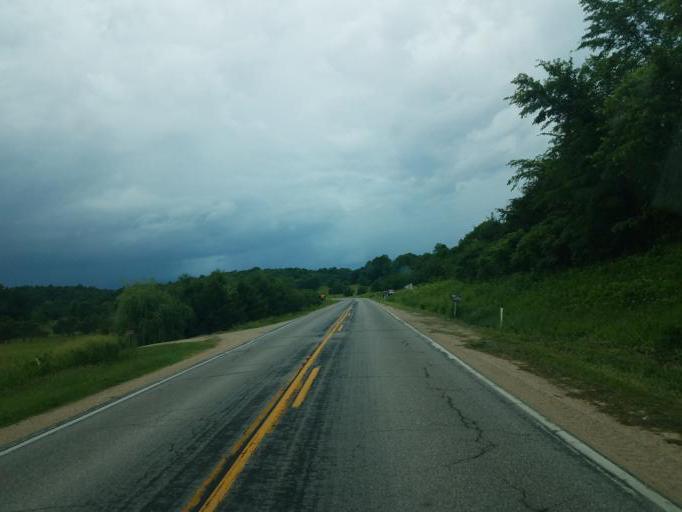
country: US
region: Wisconsin
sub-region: Vernon County
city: Hillsboro
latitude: 43.6452
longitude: -90.4296
